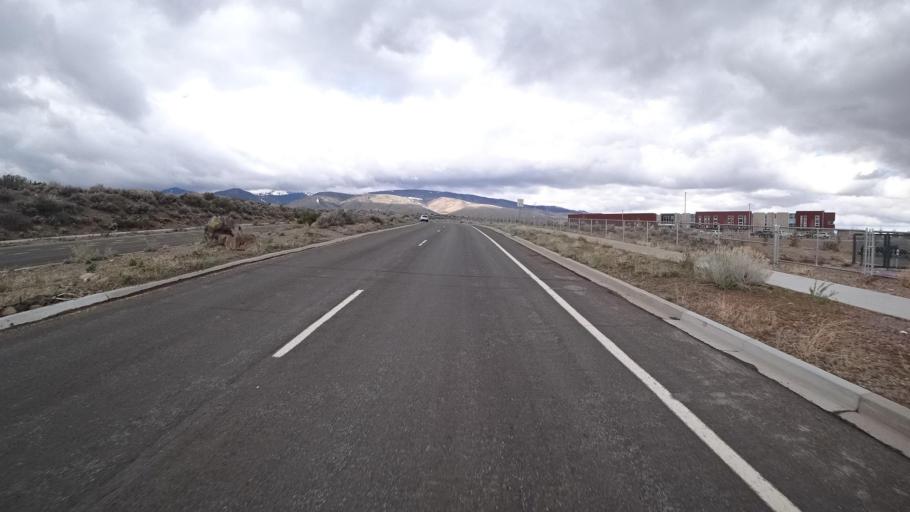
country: US
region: Nevada
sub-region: Washoe County
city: Reno
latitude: 39.4047
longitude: -119.7918
